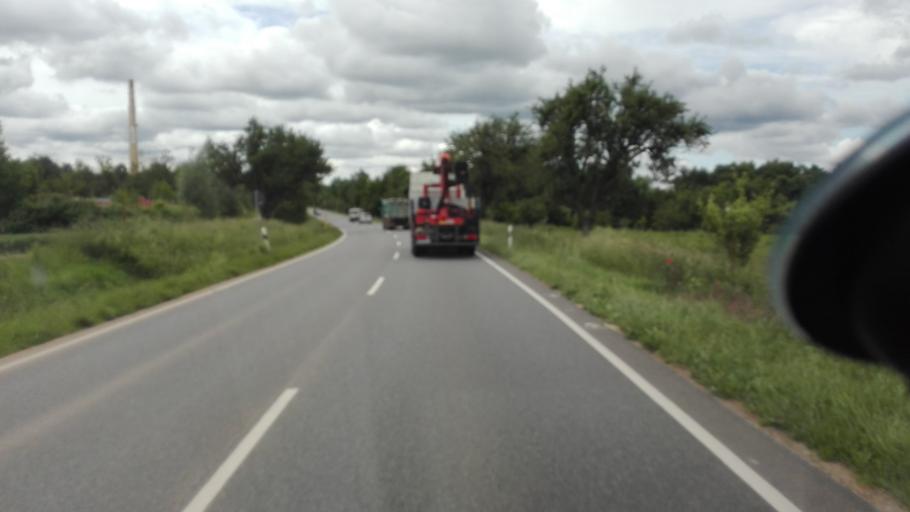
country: DE
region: Baden-Wuerttemberg
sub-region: Karlsruhe Region
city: Malsch
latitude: 49.2537
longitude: 8.6660
